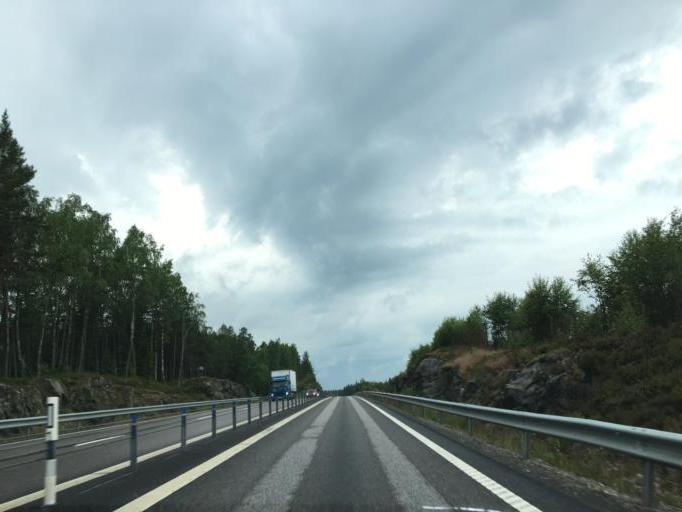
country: SE
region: OEstergoetland
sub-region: Norrkopings Kommun
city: Jursla
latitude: 58.8271
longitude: 16.1849
